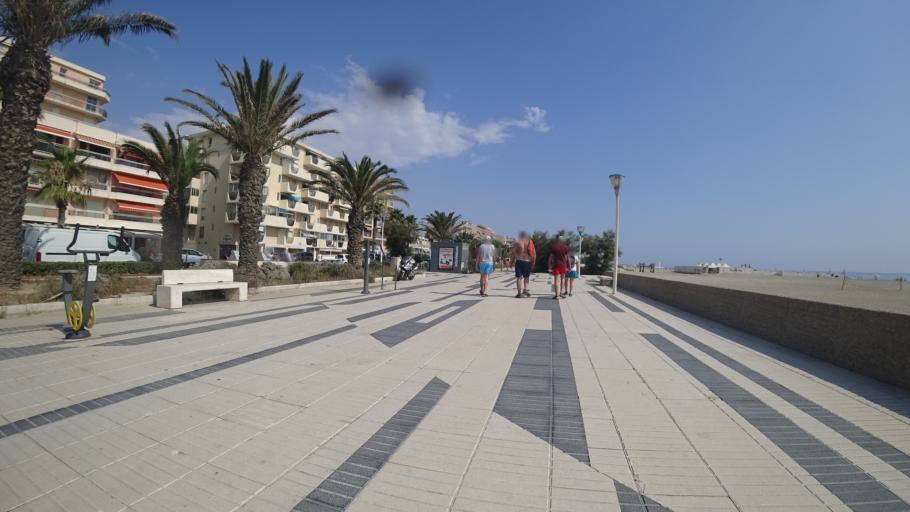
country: FR
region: Languedoc-Roussillon
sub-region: Departement des Pyrenees-Orientales
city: Canet-en-Roussillon
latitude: 42.6833
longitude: 3.0346
